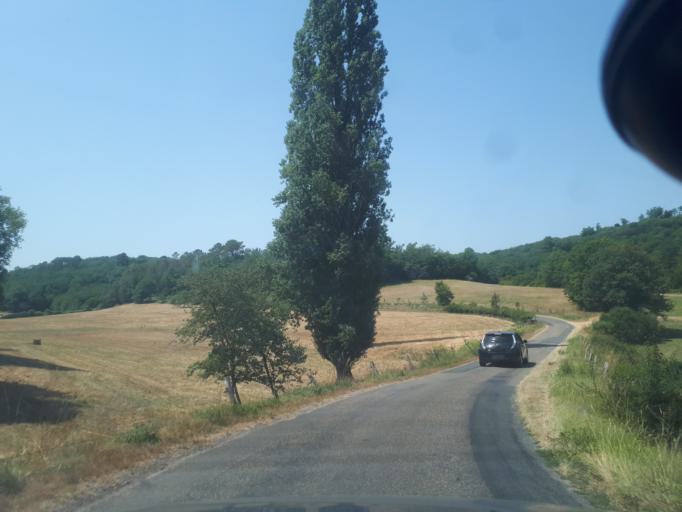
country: FR
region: Midi-Pyrenees
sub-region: Departement du Lot
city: Gourdon
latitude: 44.7495
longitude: 1.3372
